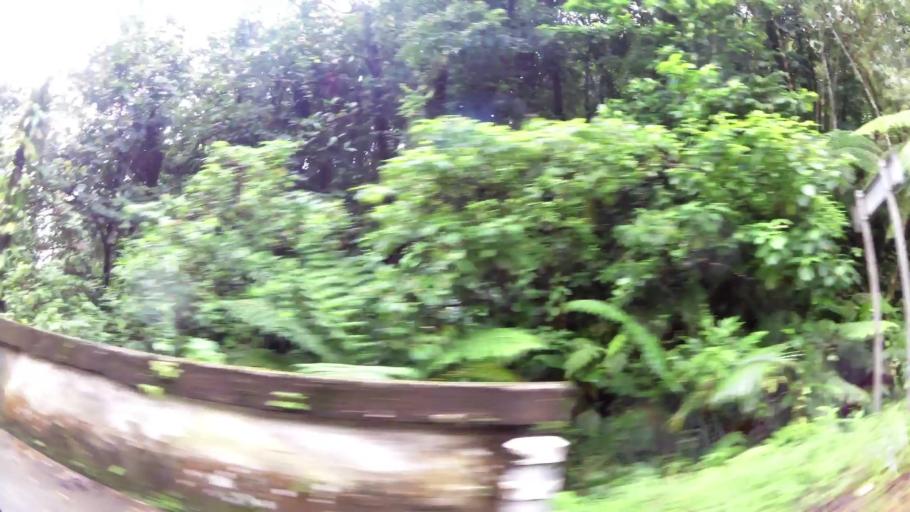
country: GP
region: Guadeloupe
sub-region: Guadeloupe
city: Trois-Rivieres
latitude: 16.0377
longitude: -61.6380
